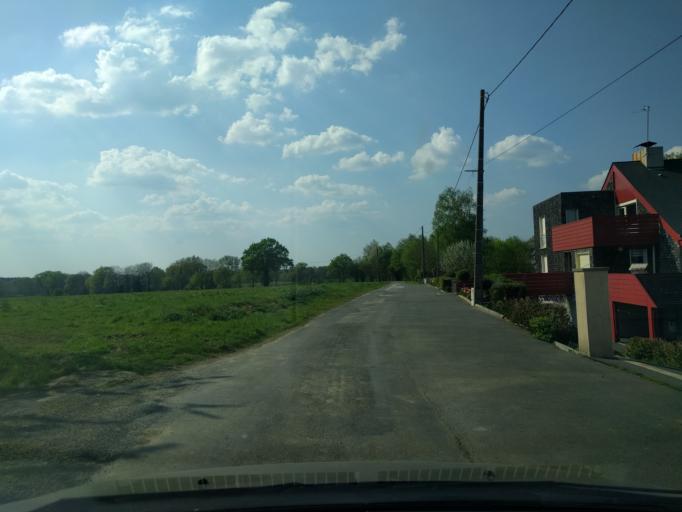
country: FR
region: Brittany
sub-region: Departement d'Ille-et-Vilaine
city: Gosne
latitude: 48.2886
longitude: -1.4539
